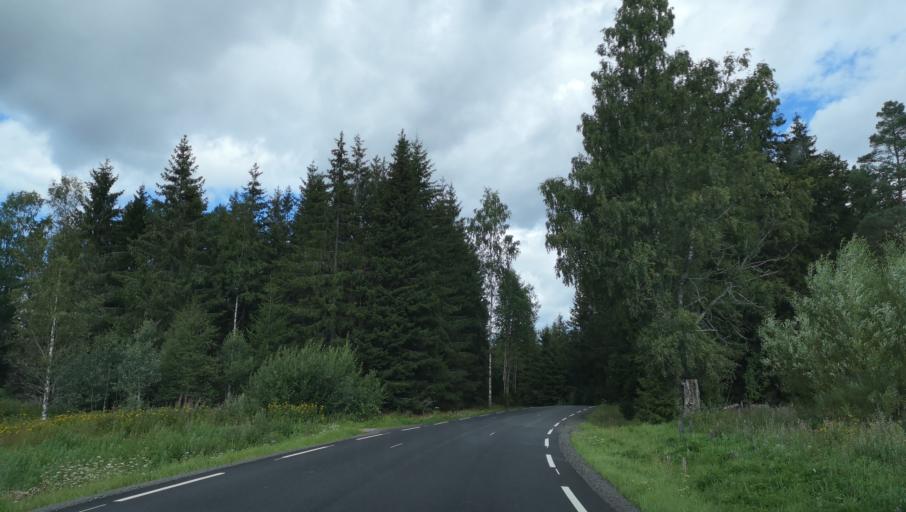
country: NO
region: Ostfold
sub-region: Hobol
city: Elvestad
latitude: 59.6906
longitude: 10.9284
